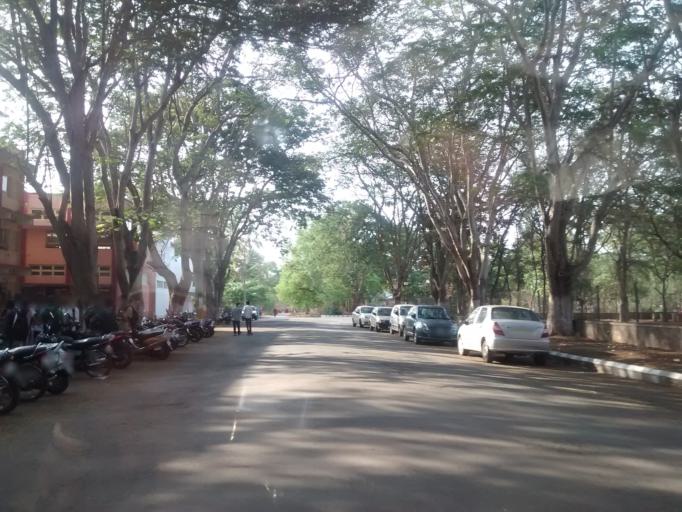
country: IN
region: Karnataka
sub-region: Dharwad
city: Hubli
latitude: 15.4414
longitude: 74.9837
